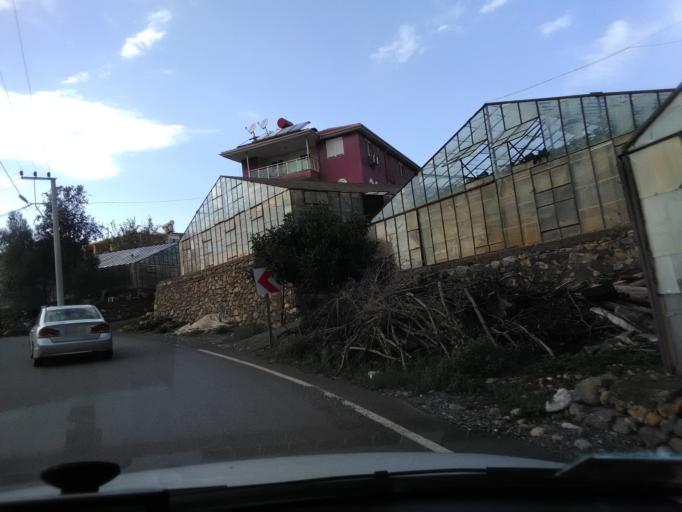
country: TR
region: Antalya
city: Gazipasa
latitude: 36.2757
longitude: 32.3475
